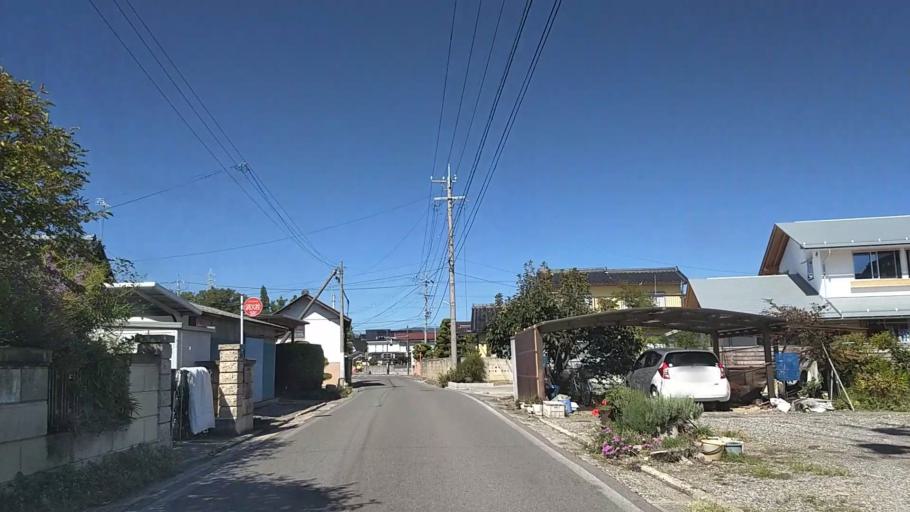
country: JP
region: Nagano
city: Nagano-shi
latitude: 36.6161
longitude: 138.1683
